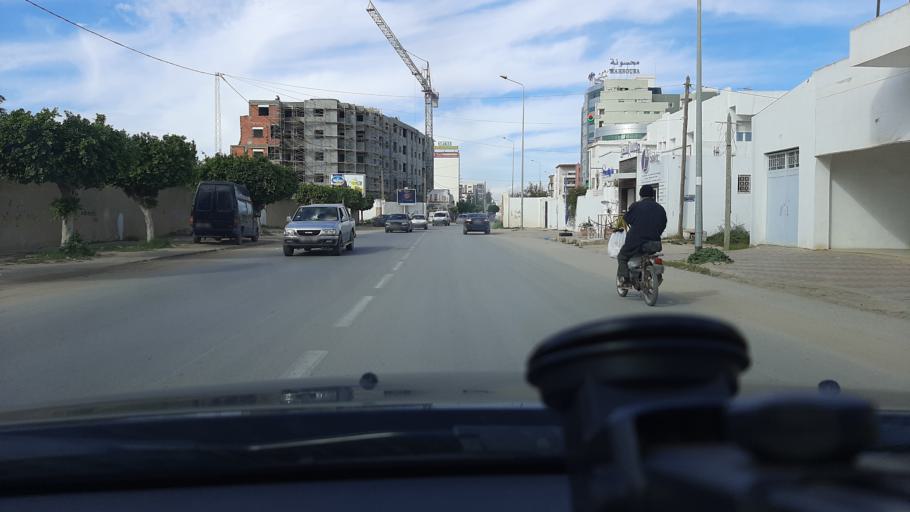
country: TN
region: Safaqis
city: Sfax
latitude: 34.7613
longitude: 10.7298
